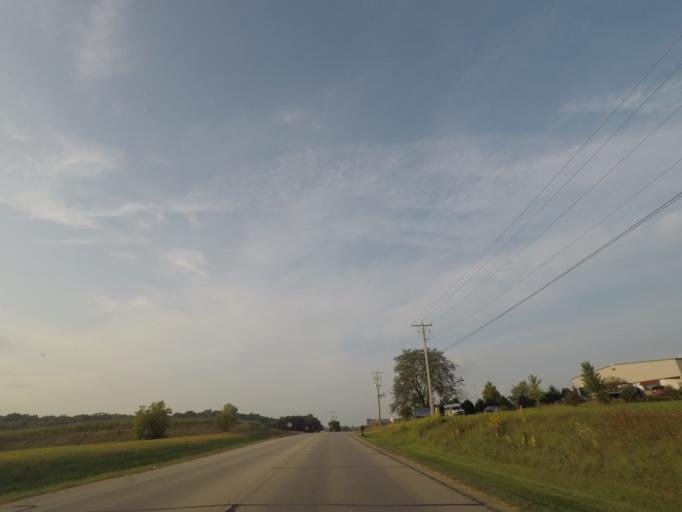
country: US
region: Wisconsin
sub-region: Dane County
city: Cottage Grove
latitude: 43.1008
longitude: -89.1995
